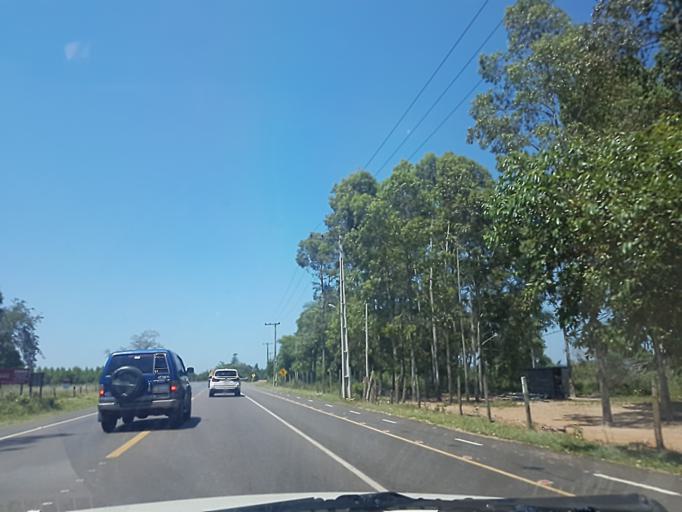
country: PY
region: Cordillera
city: San Bernardino
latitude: -25.2644
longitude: -57.3208
